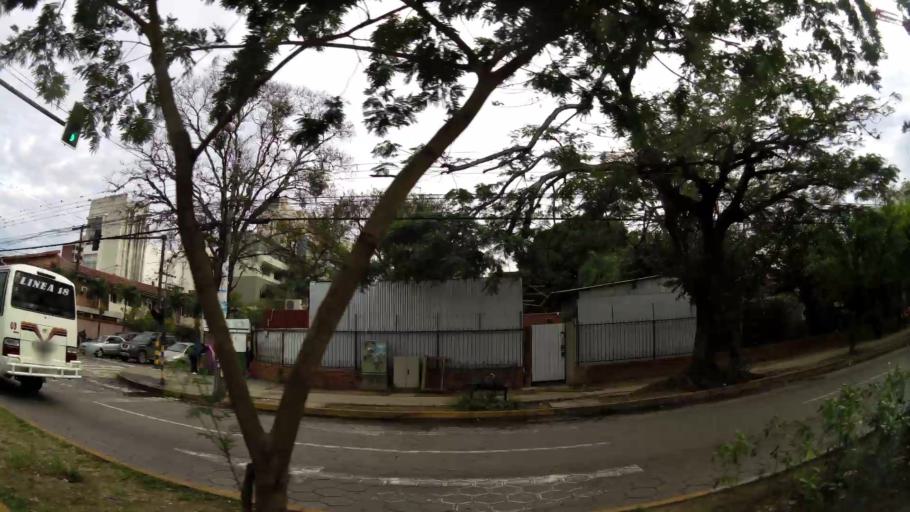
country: BO
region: Santa Cruz
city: Santa Cruz de la Sierra
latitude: -17.7921
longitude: -63.1794
